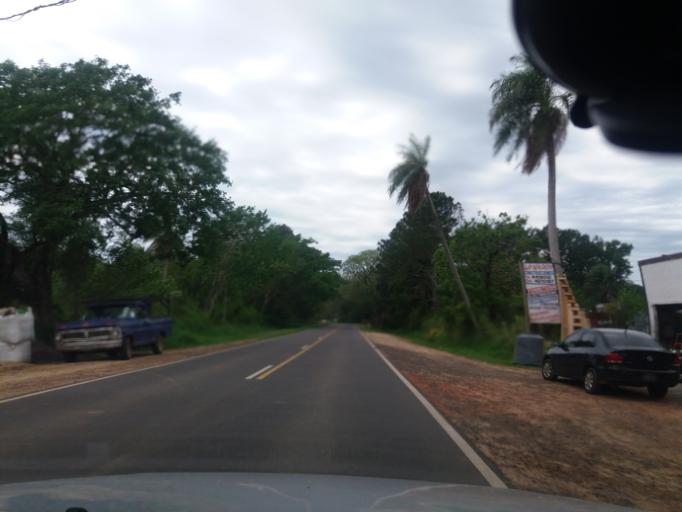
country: AR
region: Corrientes
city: Riachuelo
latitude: -27.4568
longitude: -58.6852
